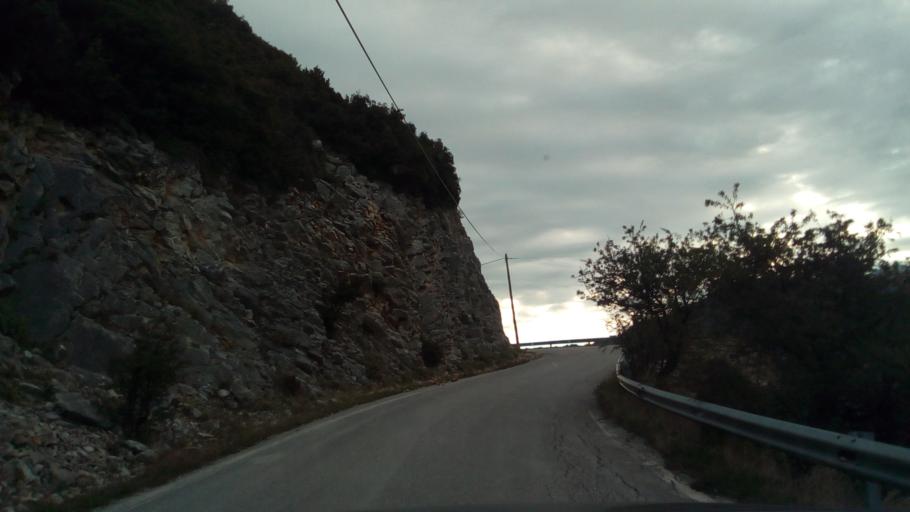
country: GR
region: West Greece
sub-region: Nomos Aitolias kai Akarnanias
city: Thermo
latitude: 38.5913
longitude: 21.8213
